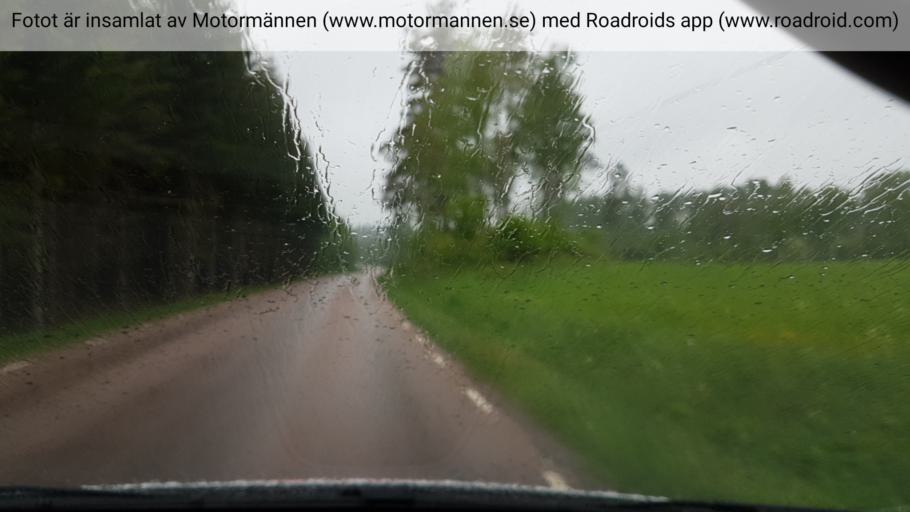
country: SE
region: Vaestra Goetaland
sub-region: Ulricehamns Kommun
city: Ulricehamn
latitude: 57.8307
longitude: 13.4642
